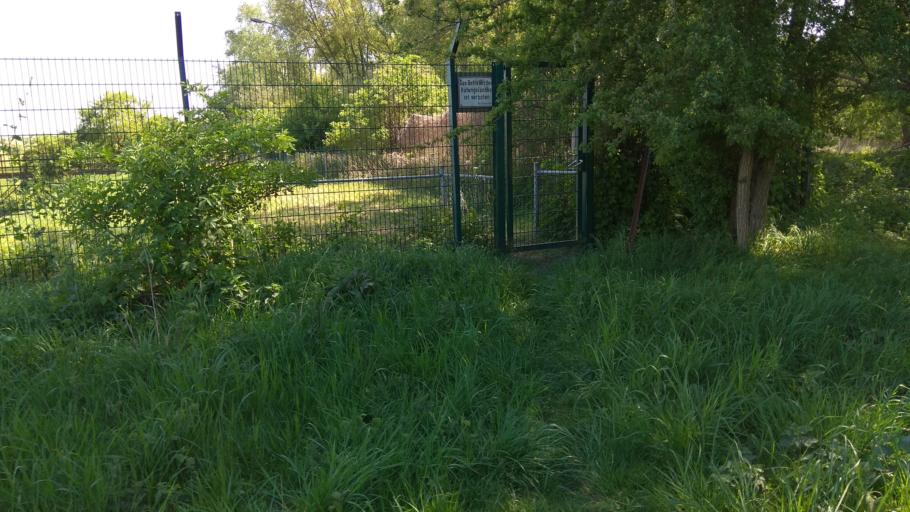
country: DE
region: North Rhine-Westphalia
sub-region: Regierungsbezirk Dusseldorf
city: Wesel
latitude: 51.6332
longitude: 6.6109
